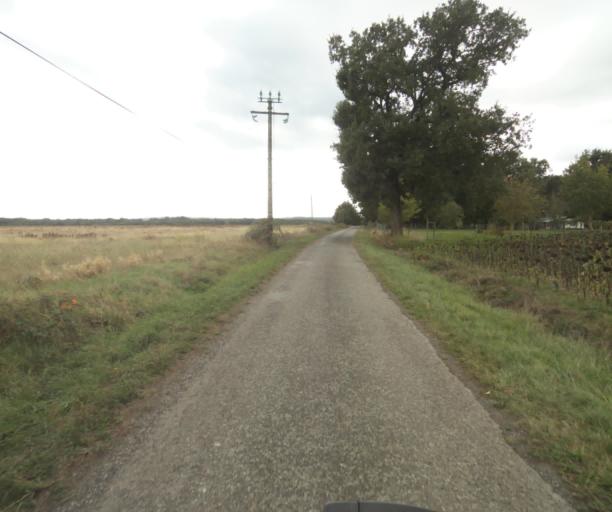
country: FR
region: Midi-Pyrenees
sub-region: Departement du Tarn-et-Garonne
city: Verdun-sur-Garonne
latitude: 43.8596
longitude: 1.1460
